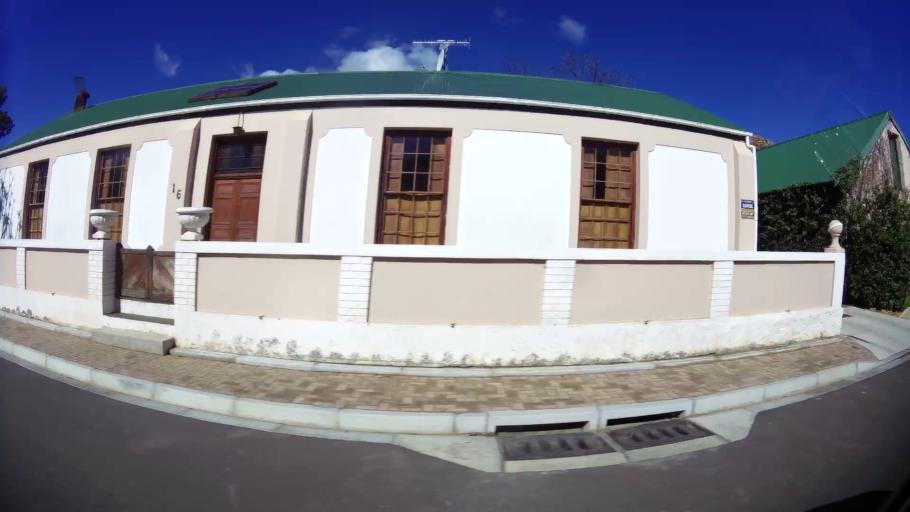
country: ZA
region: Western Cape
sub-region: Cape Winelands District Municipality
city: Ashton
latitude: -33.7908
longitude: 20.1122
